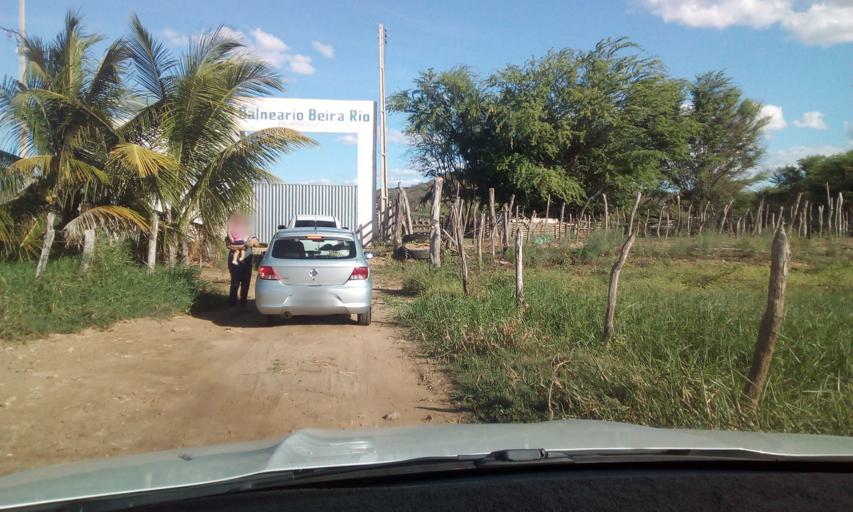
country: BR
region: Paraiba
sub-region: Picui
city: Picui
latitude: -6.5132
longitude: -36.3526
